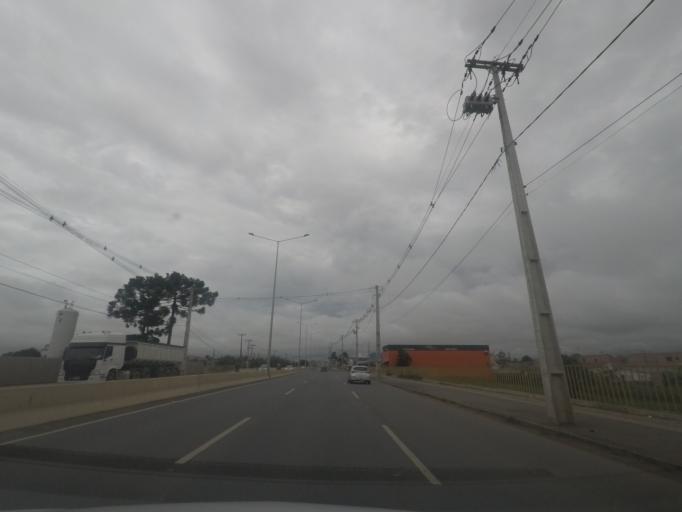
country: BR
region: Parana
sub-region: Pinhais
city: Pinhais
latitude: -25.4412
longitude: -49.1523
